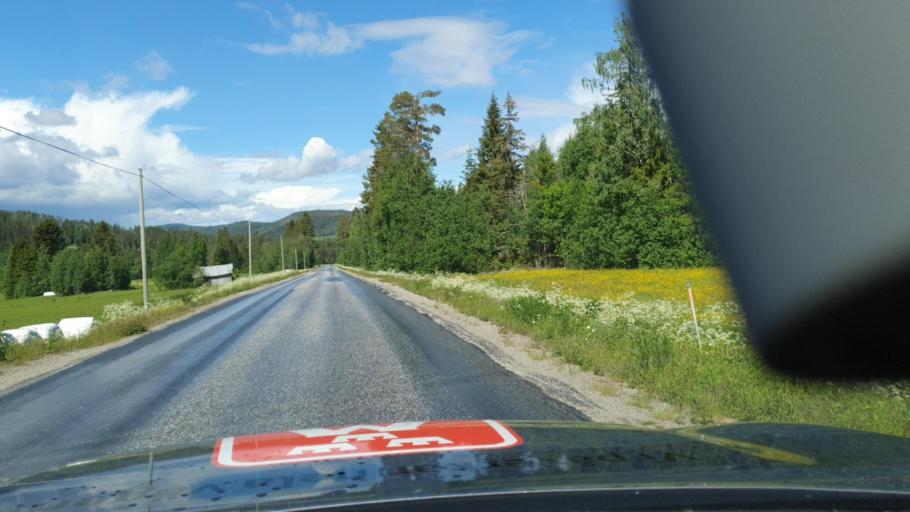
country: SE
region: Vaesternorrland
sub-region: OErnskoeldsviks Kommun
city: Bredbyn
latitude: 63.3459
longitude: 18.0067
